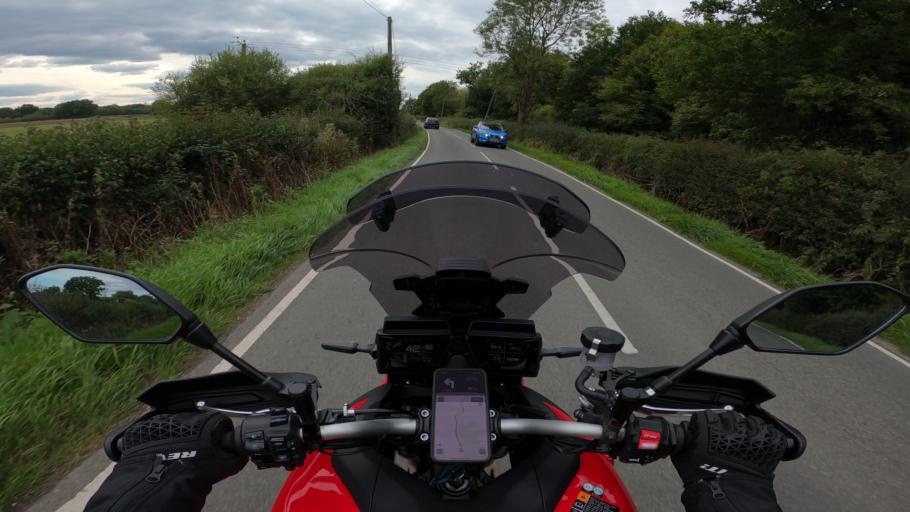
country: GB
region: England
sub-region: Surrey
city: Lingfield
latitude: 51.1899
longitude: 0.0181
